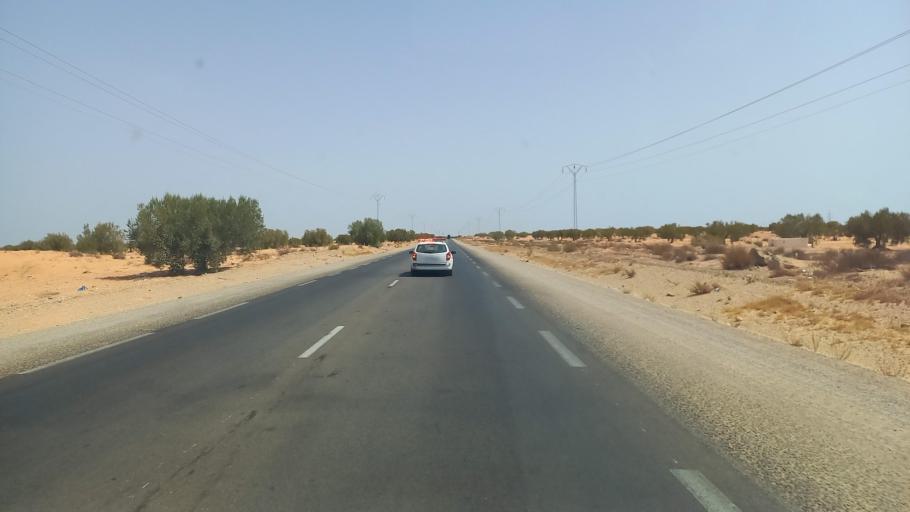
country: TN
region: Madanin
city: Zarzis
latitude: 33.4184
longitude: 10.8754
